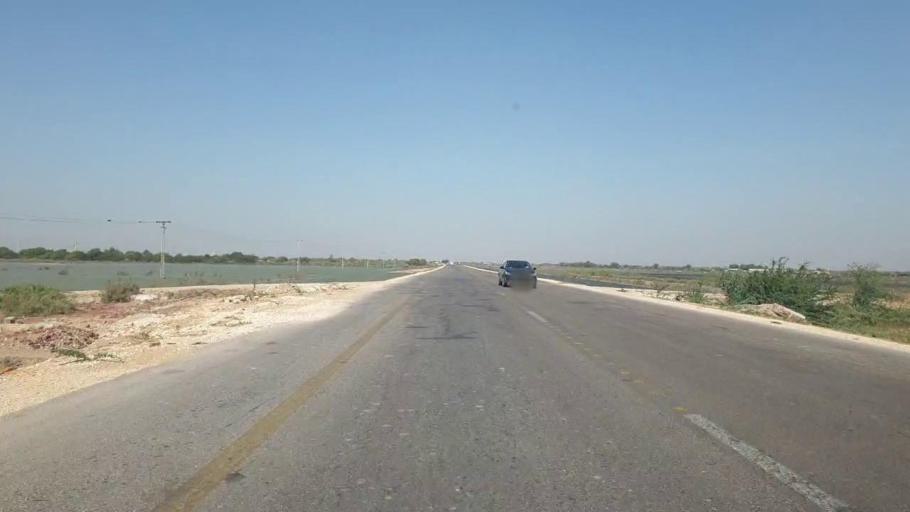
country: PK
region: Sindh
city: Talhar
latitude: 24.8367
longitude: 68.8161
